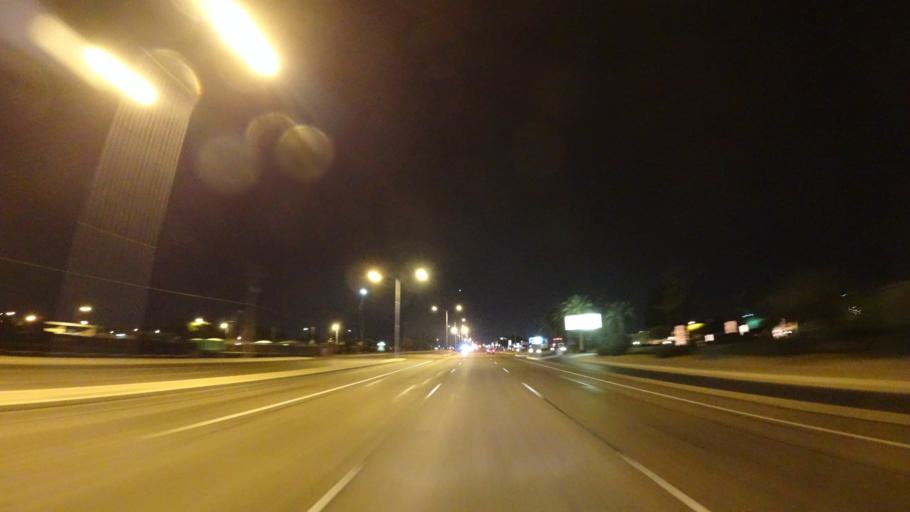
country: US
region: Arizona
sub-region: Maricopa County
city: Gilbert
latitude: 33.4156
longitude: -111.7287
